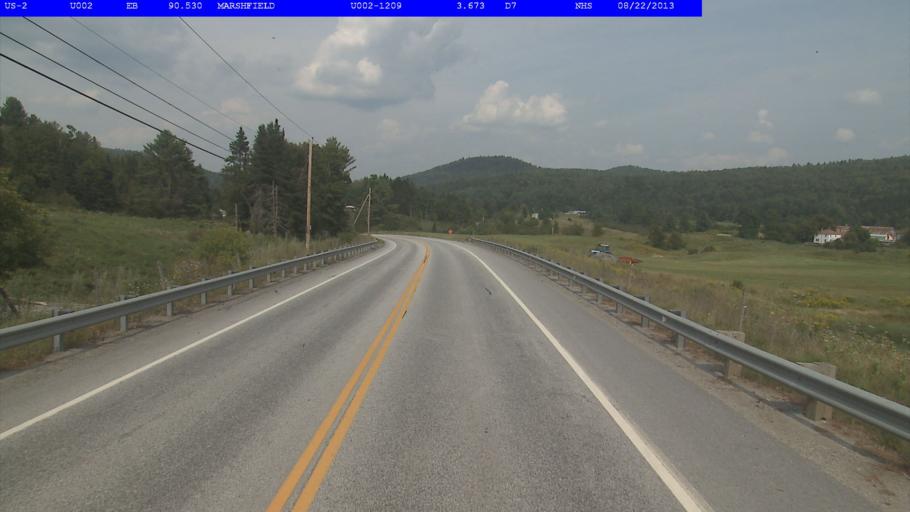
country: US
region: Vermont
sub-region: Washington County
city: Barre
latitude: 44.3190
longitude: -72.3840
